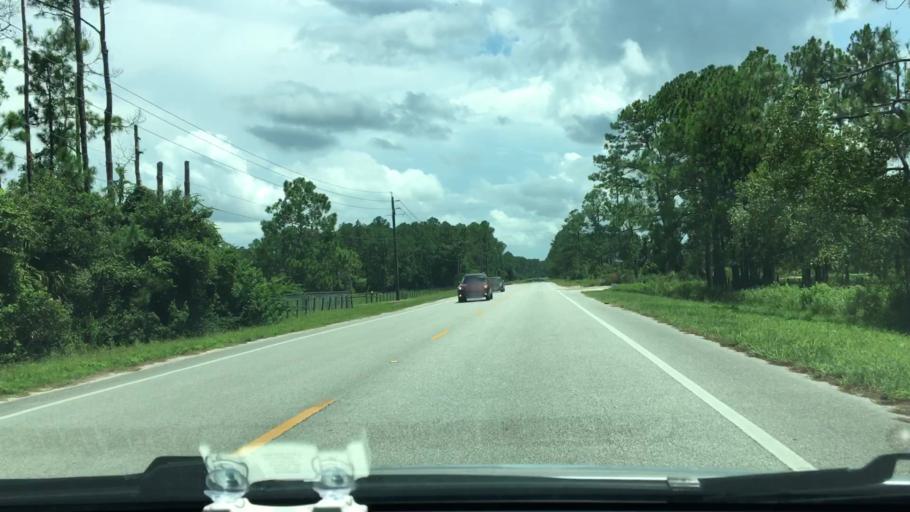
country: US
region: Florida
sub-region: Volusia County
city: Samsula-Spruce Creek
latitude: 29.0371
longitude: -81.0670
